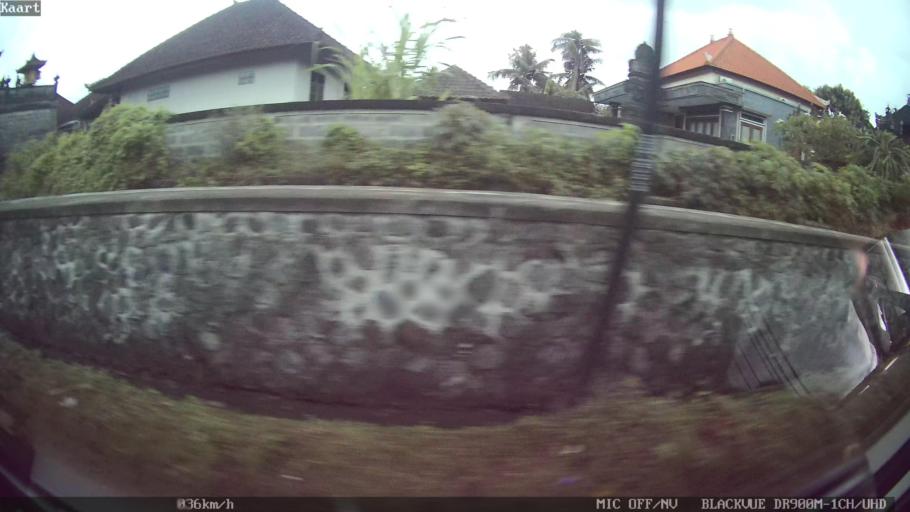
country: ID
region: Bali
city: Banjar Batur
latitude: -8.6010
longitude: 115.2059
